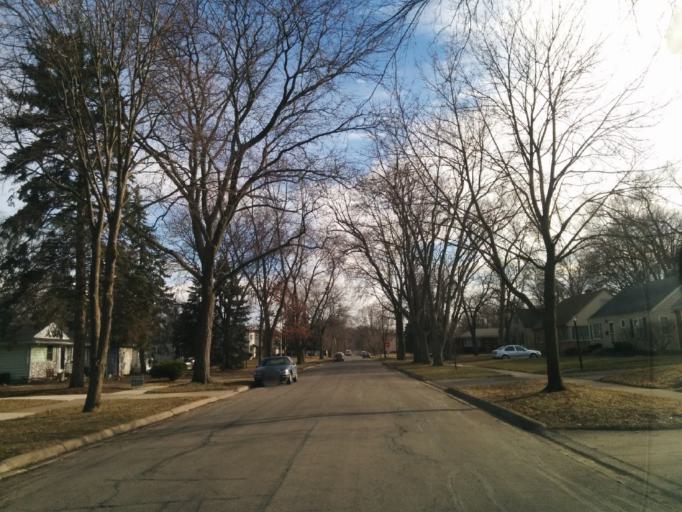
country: US
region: Illinois
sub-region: DuPage County
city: Lombard
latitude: 41.8853
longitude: -87.9993
